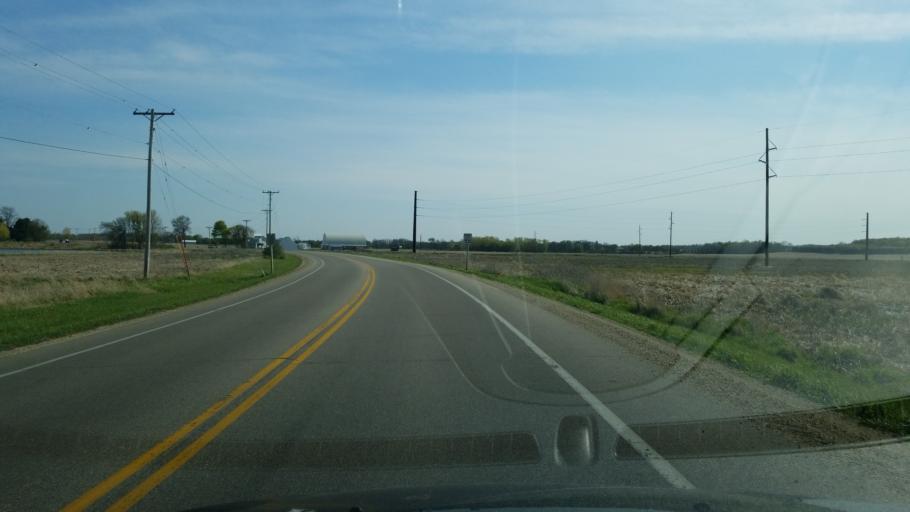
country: US
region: Wisconsin
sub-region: Dane County
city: Fitchburg
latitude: 42.9454
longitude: -89.4382
